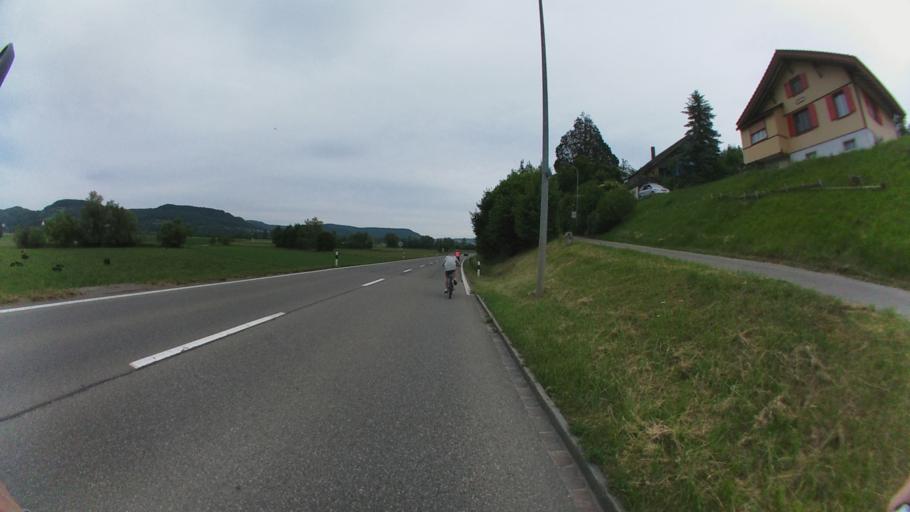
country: CH
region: Aargau
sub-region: Bezirk Zurzach
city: Bad Zurzach
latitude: 47.5999
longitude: 8.2804
